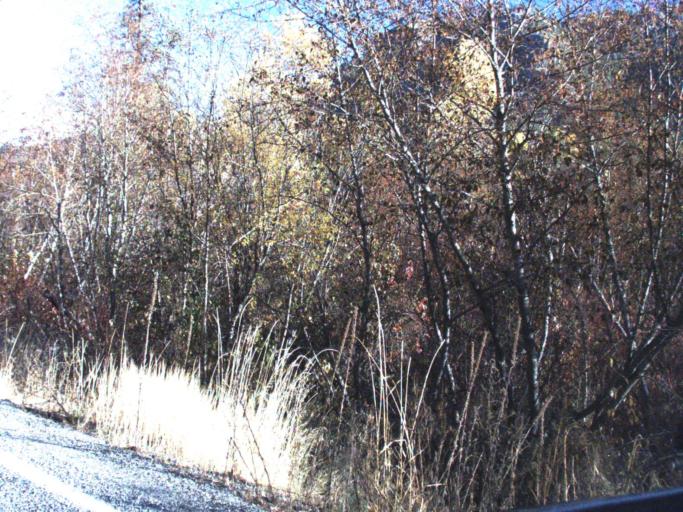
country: US
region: Washington
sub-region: Ferry County
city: Republic
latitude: 48.3311
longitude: -118.7463
